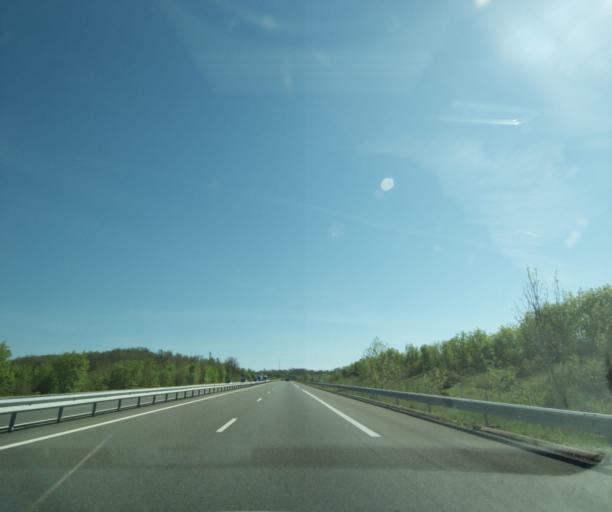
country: FR
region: Midi-Pyrenees
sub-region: Departement du Lot
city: Lalbenque
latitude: 44.2599
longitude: 1.5073
